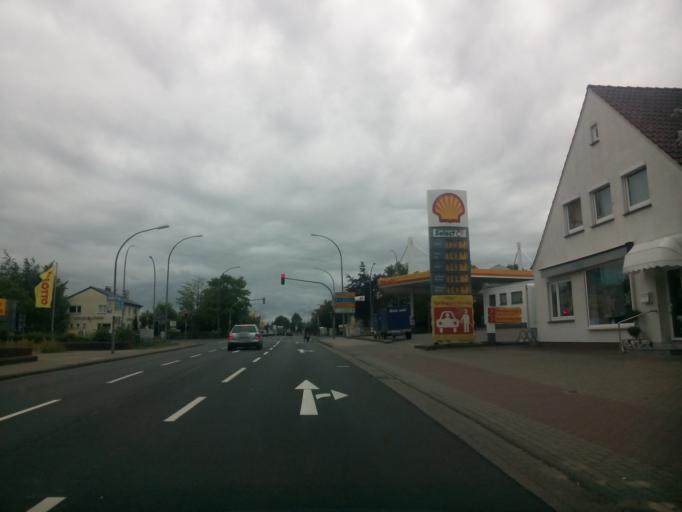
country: DE
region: Lower Saxony
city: Schwanewede
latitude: 53.2261
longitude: 8.5941
